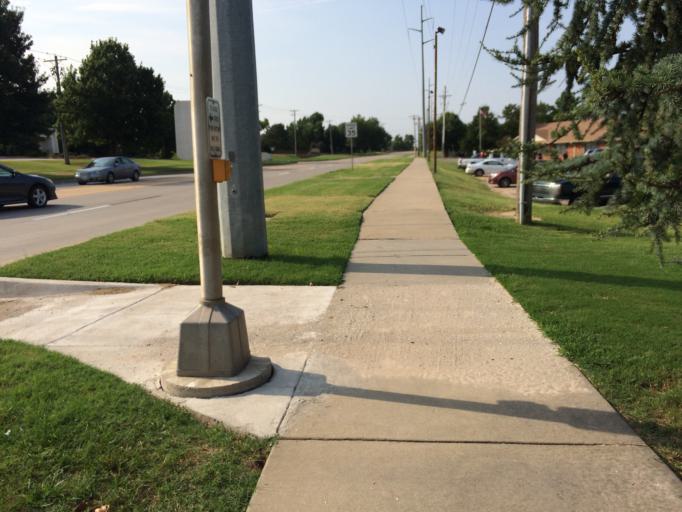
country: US
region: Oklahoma
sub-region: Cleveland County
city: Norman
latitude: 35.2113
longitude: -97.4769
